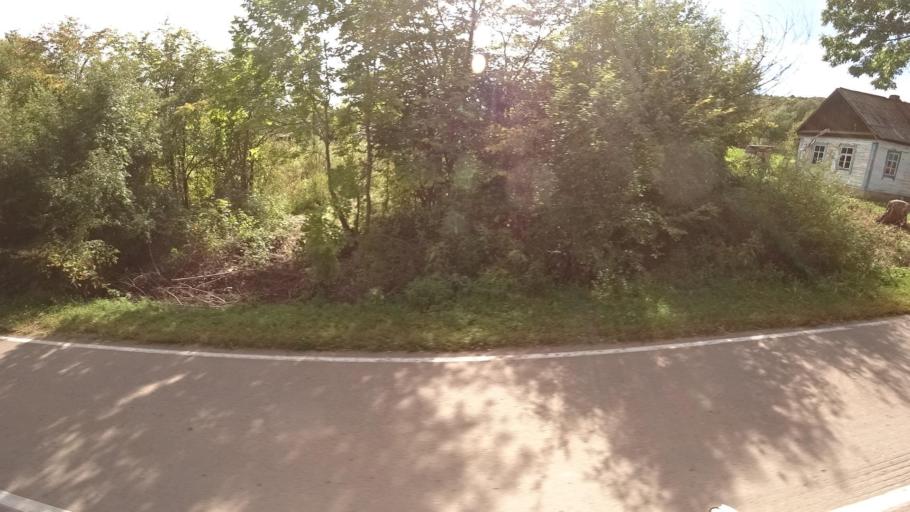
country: RU
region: Primorskiy
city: Yakovlevka
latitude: 44.3979
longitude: 133.6007
